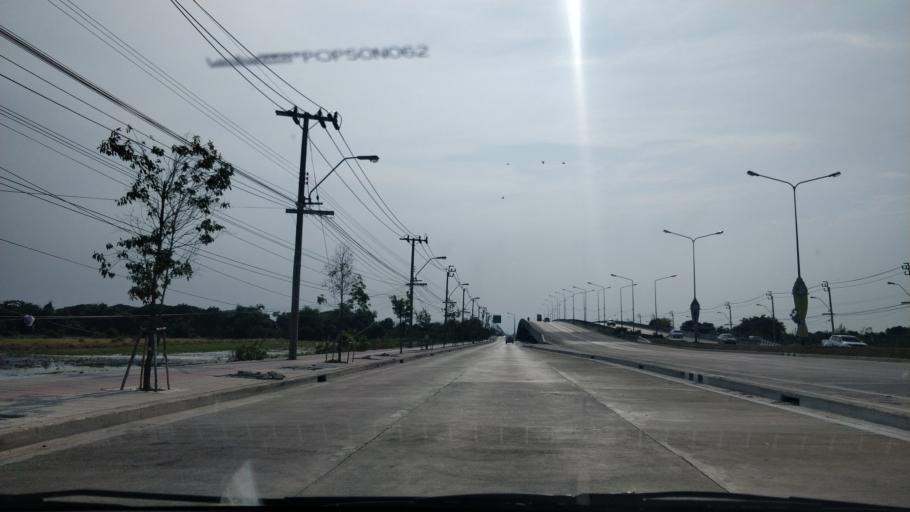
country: TH
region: Bangkok
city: Lat Krabang
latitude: 13.7556
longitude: 100.7420
